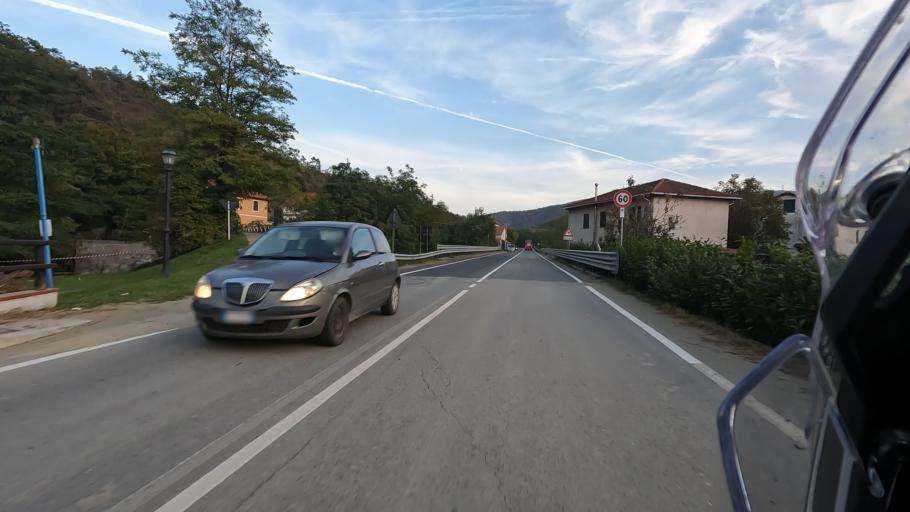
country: IT
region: Liguria
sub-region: Provincia di Savona
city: Pontinvrea
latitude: 44.4408
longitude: 8.4387
